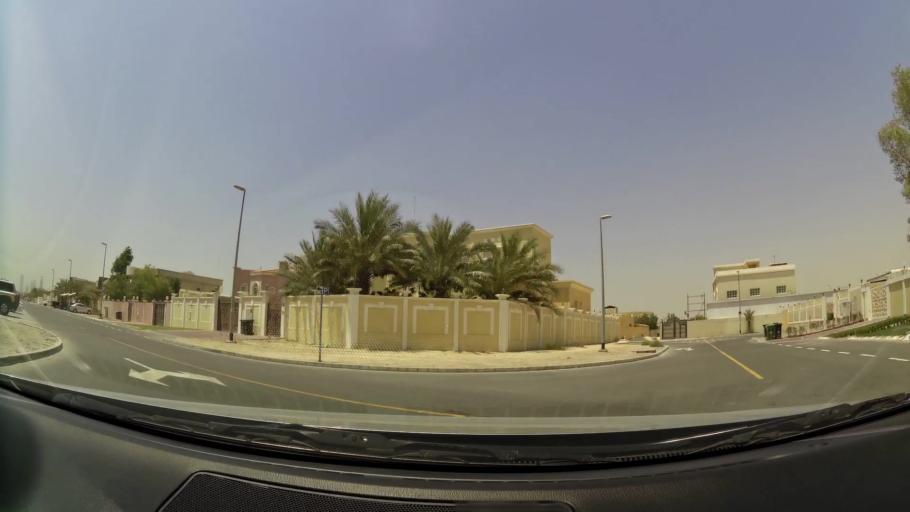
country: AE
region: Dubai
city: Dubai
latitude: 25.0836
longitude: 55.2095
